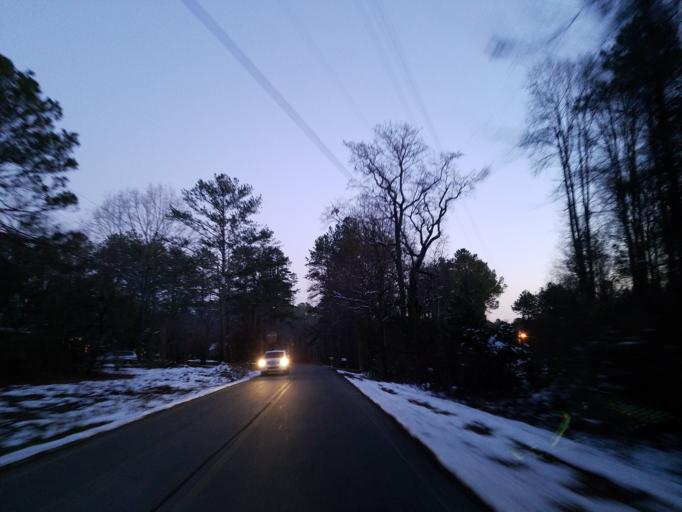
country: US
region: Georgia
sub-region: Cherokee County
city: Ball Ground
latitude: 34.3557
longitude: -84.3633
